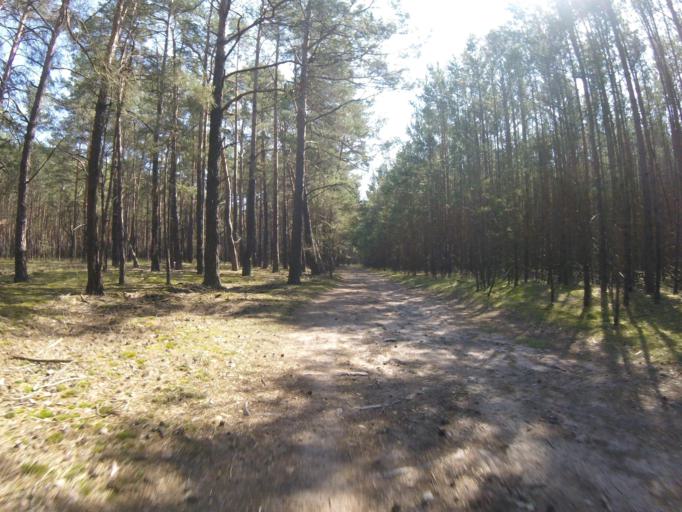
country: DE
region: Brandenburg
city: Bestensee
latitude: 52.2622
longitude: 13.6861
